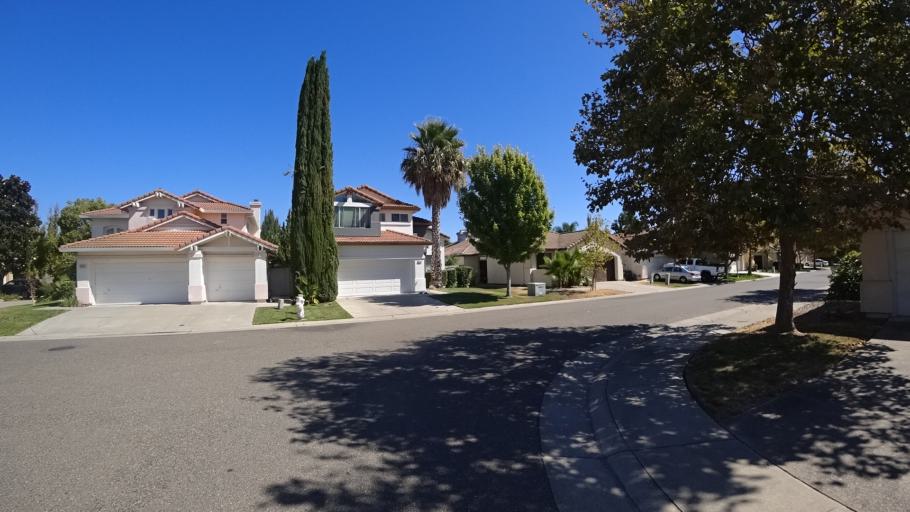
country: US
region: California
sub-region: Sacramento County
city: Laguna
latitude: 38.4218
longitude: -121.4665
